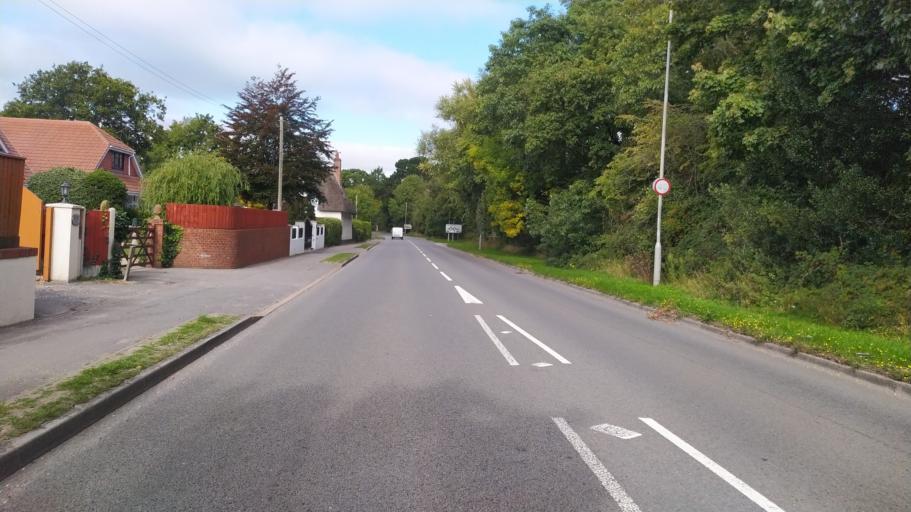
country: GB
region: England
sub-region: Dorset
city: Ferndown
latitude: 50.7859
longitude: -1.9037
